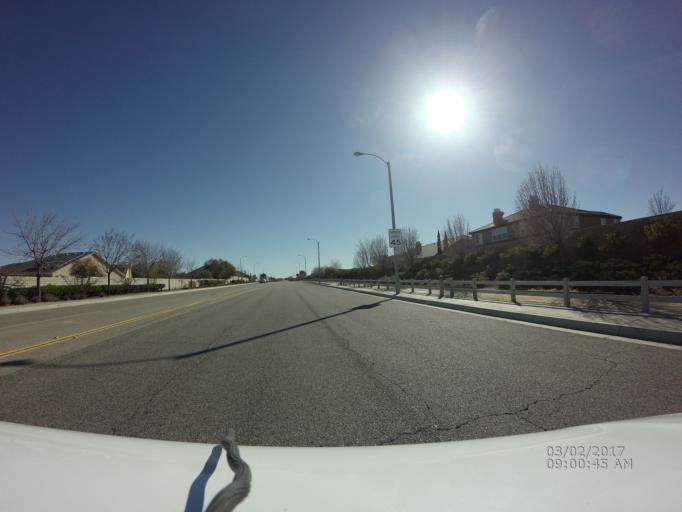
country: US
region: California
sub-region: Los Angeles County
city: Quartz Hill
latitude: 34.6382
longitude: -118.2095
